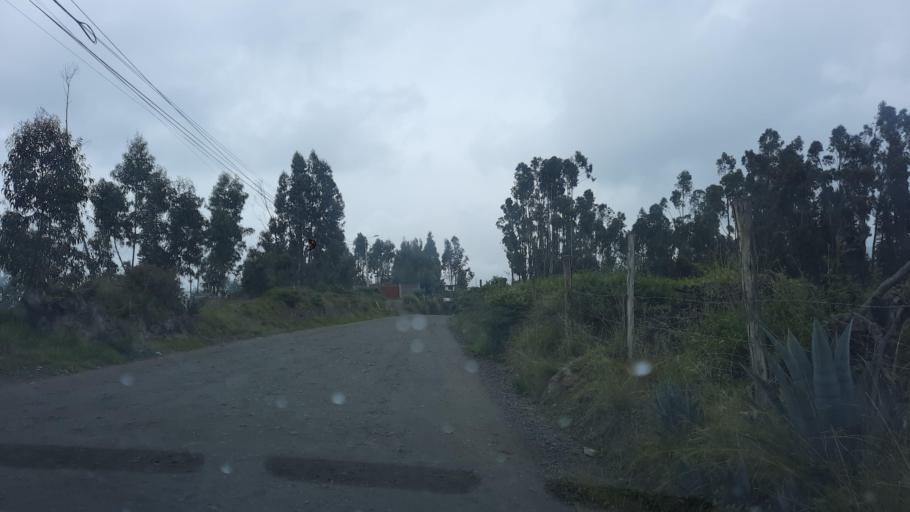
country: EC
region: Chimborazo
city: Riobamba
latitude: -1.6875
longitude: -78.6562
